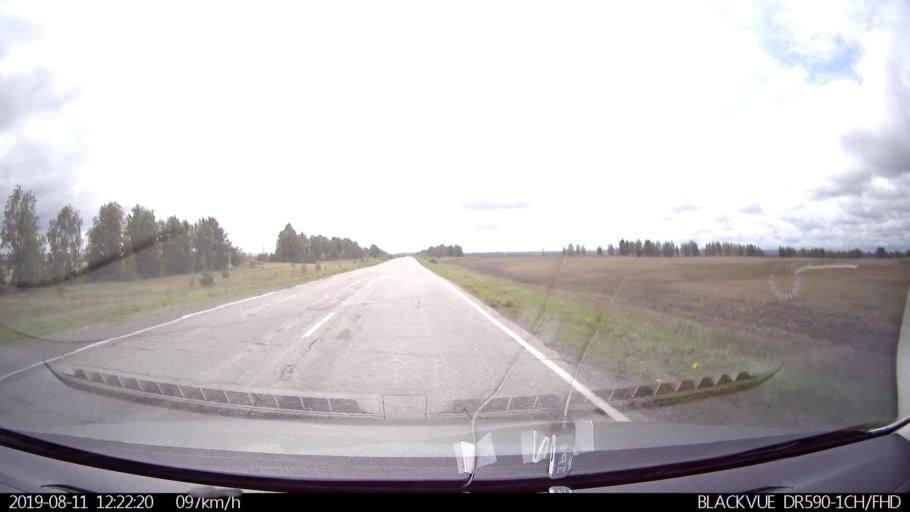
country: RU
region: Ulyanovsk
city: Ignatovka
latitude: 53.9095
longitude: 47.9554
